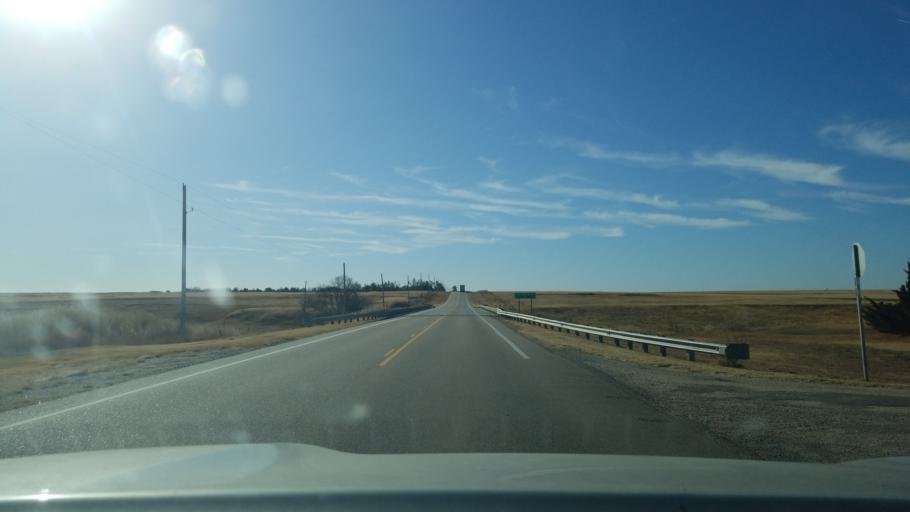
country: US
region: Kansas
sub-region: Ness County
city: Ness City
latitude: 38.4079
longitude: -99.8985
